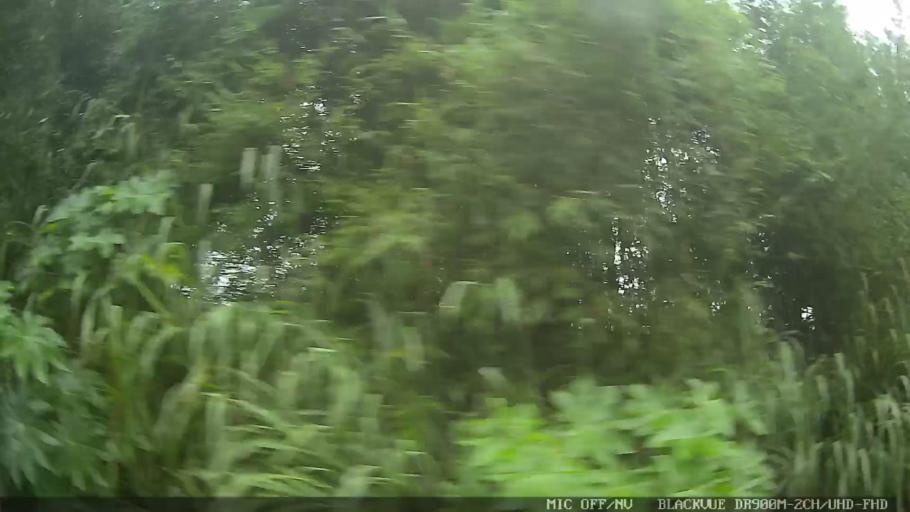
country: BR
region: Sao Paulo
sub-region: Suzano
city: Suzano
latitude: -23.6472
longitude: -46.2690
